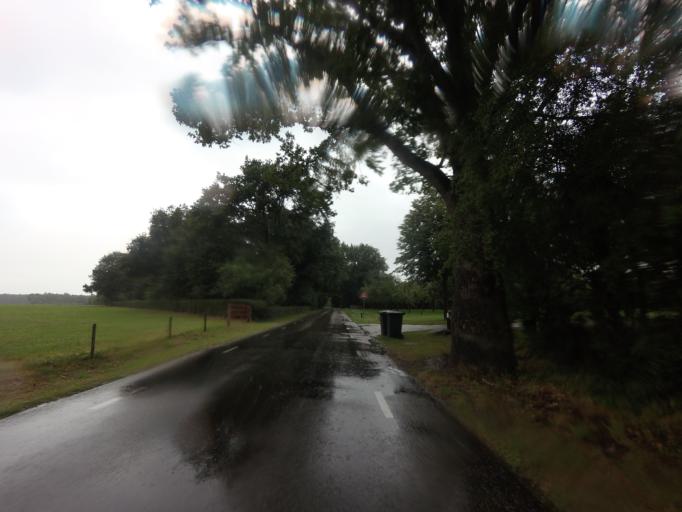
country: NL
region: Drenthe
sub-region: Gemeente Hoogeveen
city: Hoogeveen
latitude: 52.6410
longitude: 6.4456
